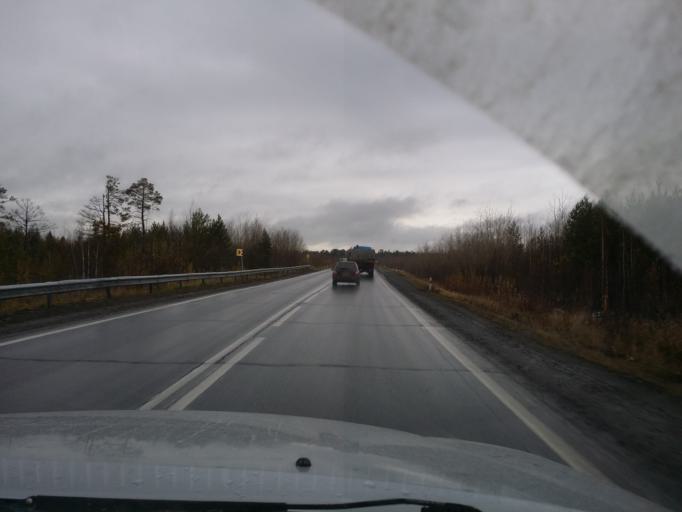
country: RU
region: Khanty-Mansiyskiy Avtonomnyy Okrug
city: Langepas
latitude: 61.1775
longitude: 75.4932
